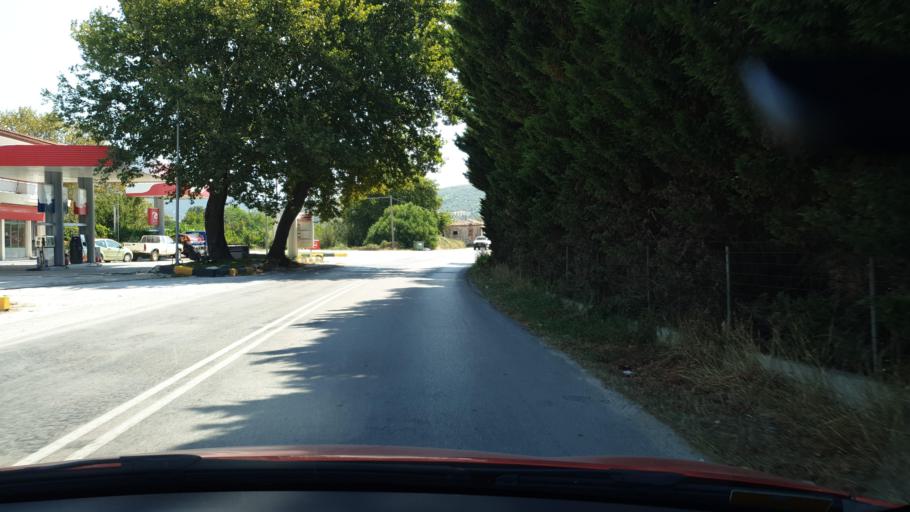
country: GR
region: Central Greece
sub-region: Nomos Evvoias
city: Oxilithos
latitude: 38.4974
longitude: 24.1112
